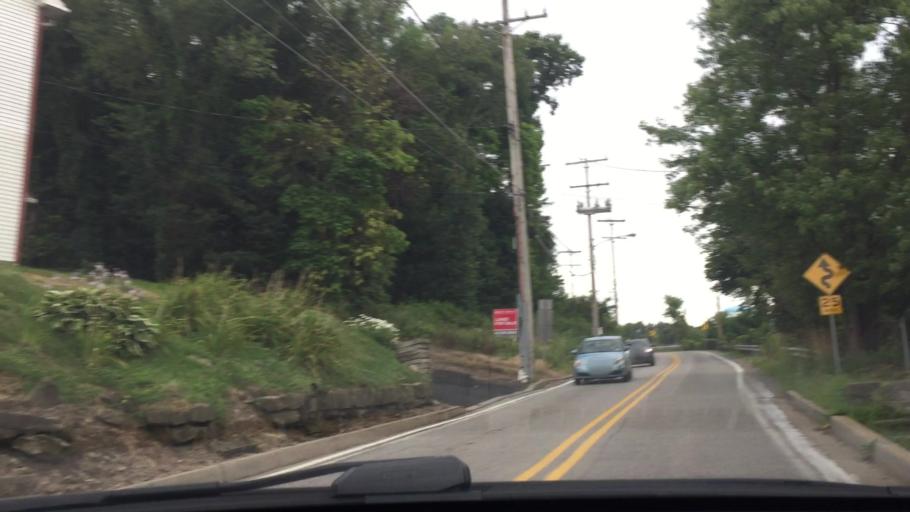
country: US
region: Pennsylvania
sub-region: Allegheny County
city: Castle Shannon
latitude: 40.3656
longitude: -80.0164
